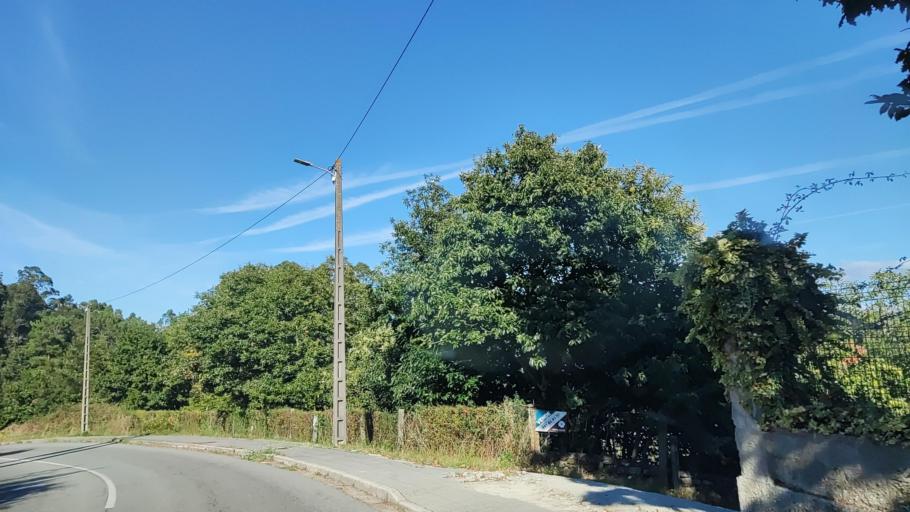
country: ES
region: Galicia
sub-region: Provincia da Coruna
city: Boiro
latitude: 42.6545
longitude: -8.8813
